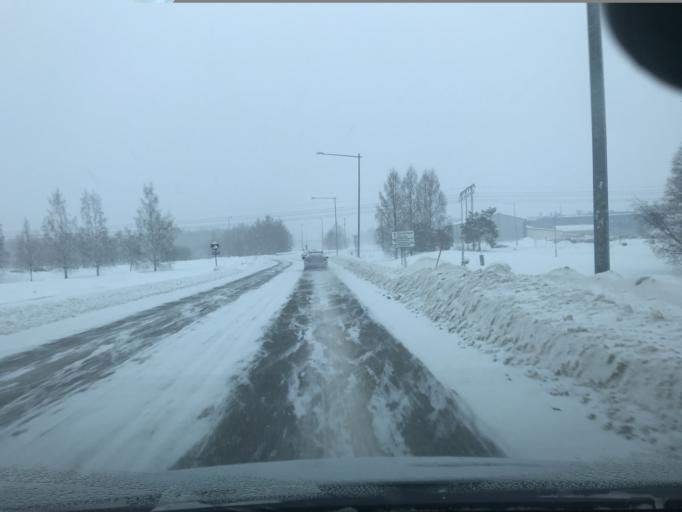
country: SE
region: Norrbotten
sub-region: Lulea Kommun
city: Lulea
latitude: 65.6170
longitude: 22.1311
